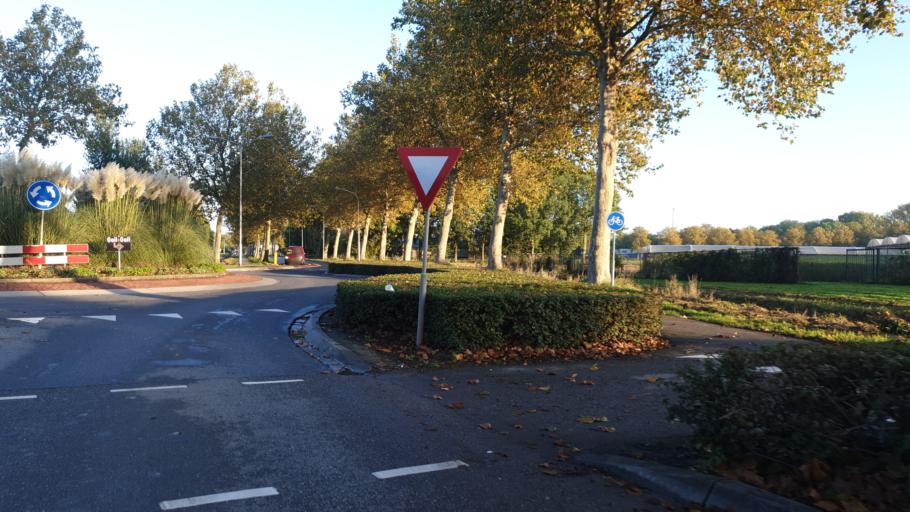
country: NL
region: Gelderland
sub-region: Gemeente Druten
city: Druten
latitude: 51.8798
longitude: 5.6106
